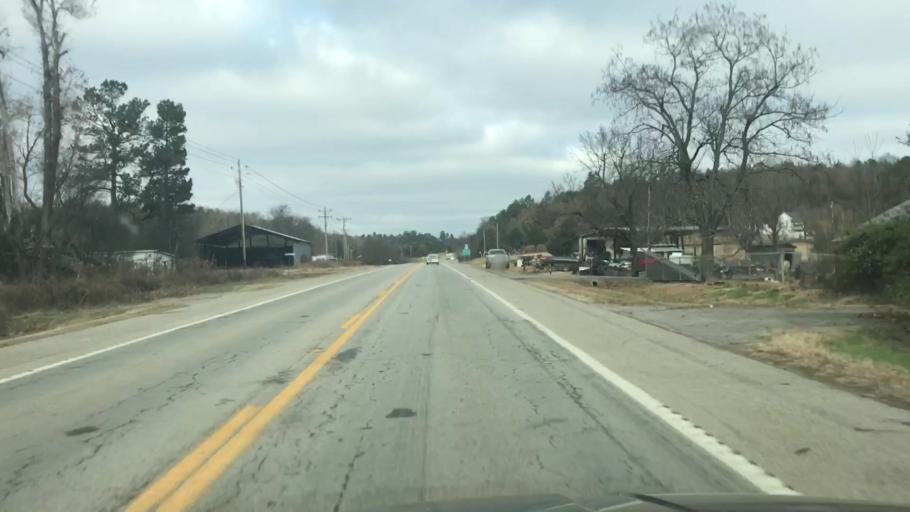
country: US
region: Arkansas
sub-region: Scott County
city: Waldron
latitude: 34.8511
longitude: -94.0625
